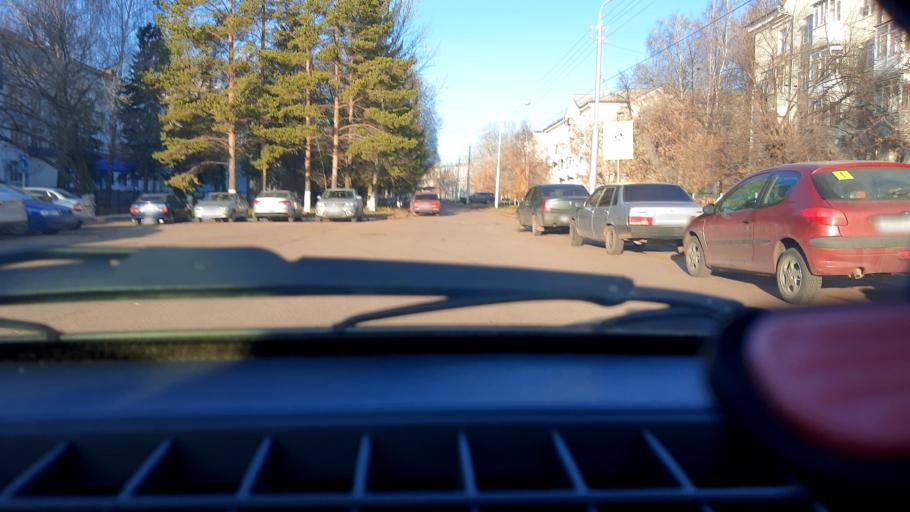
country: RU
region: Bashkortostan
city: Ufa
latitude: 54.8163
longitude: 56.0669
